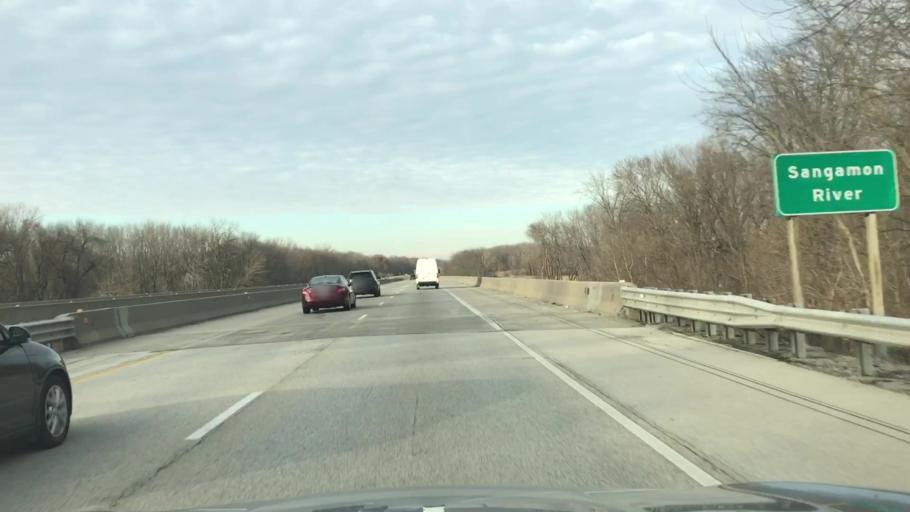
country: US
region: Illinois
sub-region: Sangamon County
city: Sherman
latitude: 39.8701
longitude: -89.5960
